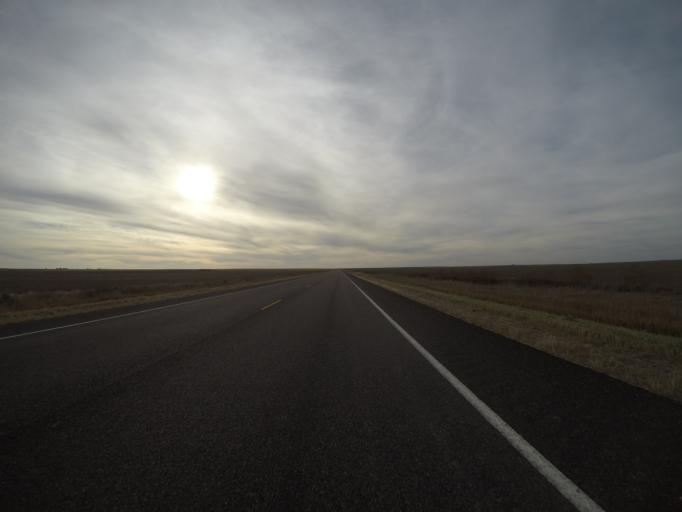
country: US
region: Kansas
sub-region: Cheyenne County
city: Saint Francis
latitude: 39.7462
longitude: -102.1087
